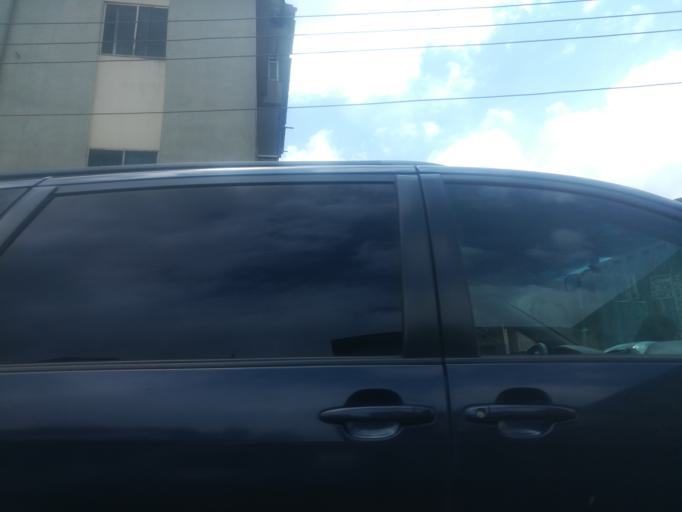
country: NG
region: Lagos
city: Ojota
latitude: 6.5994
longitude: 3.3887
